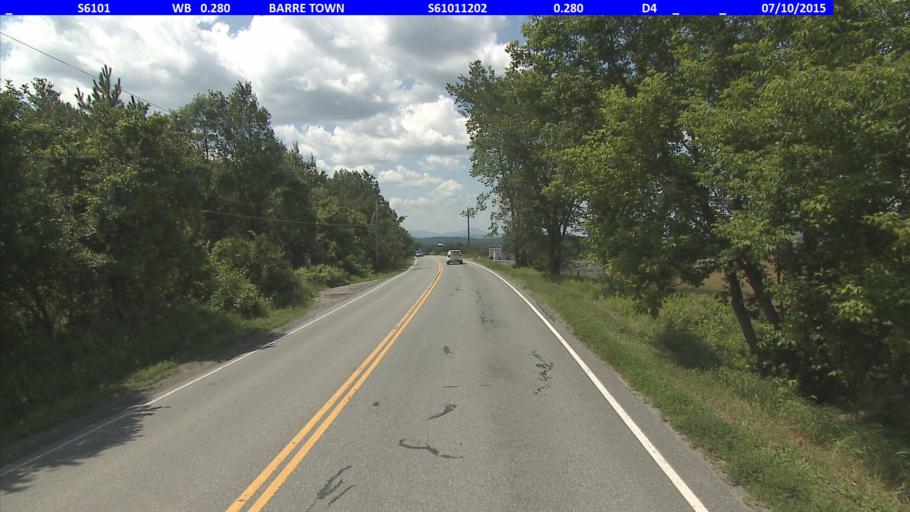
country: US
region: Vermont
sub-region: Washington County
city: South Barre
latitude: 44.1890
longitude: -72.5405
